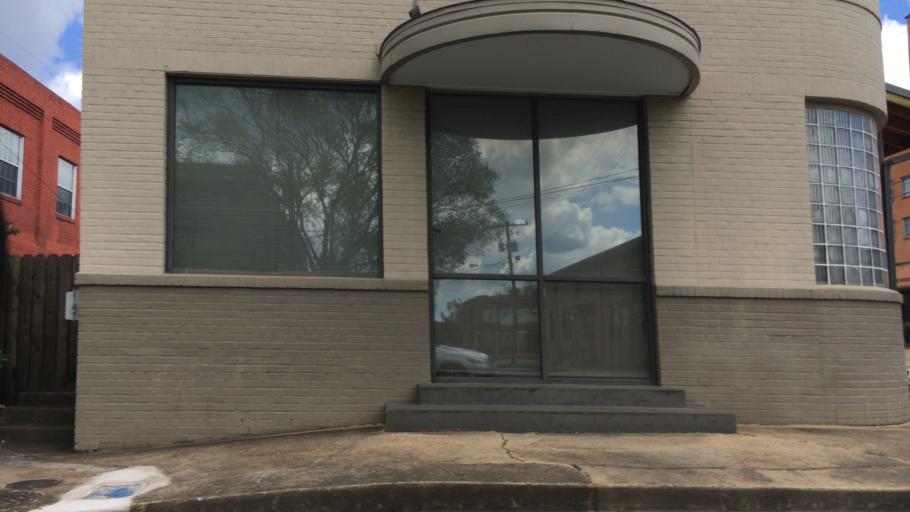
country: US
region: Louisiana
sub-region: Lincoln Parish
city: Ruston
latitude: 32.5277
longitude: -92.6393
